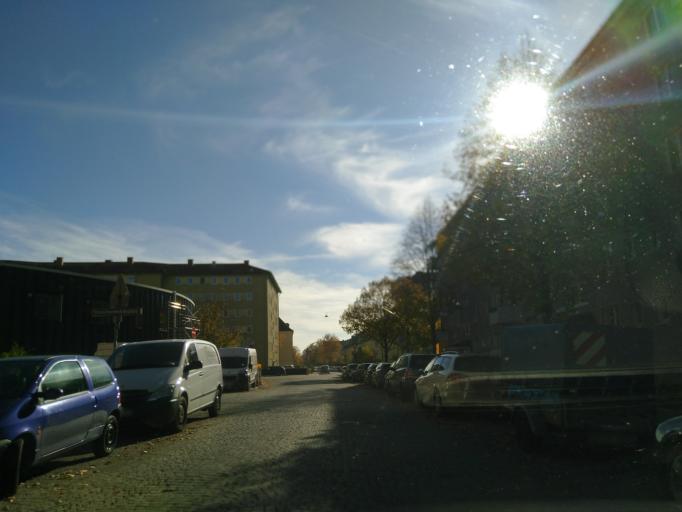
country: DE
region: Bavaria
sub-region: Upper Bavaria
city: Munich
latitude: 48.1060
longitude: 11.5910
